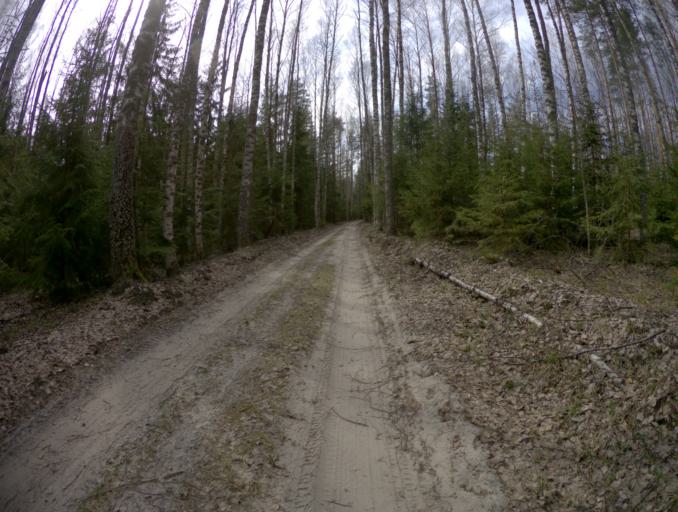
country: RU
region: Vladimir
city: Urshel'skiy
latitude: 55.8661
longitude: 40.1995
